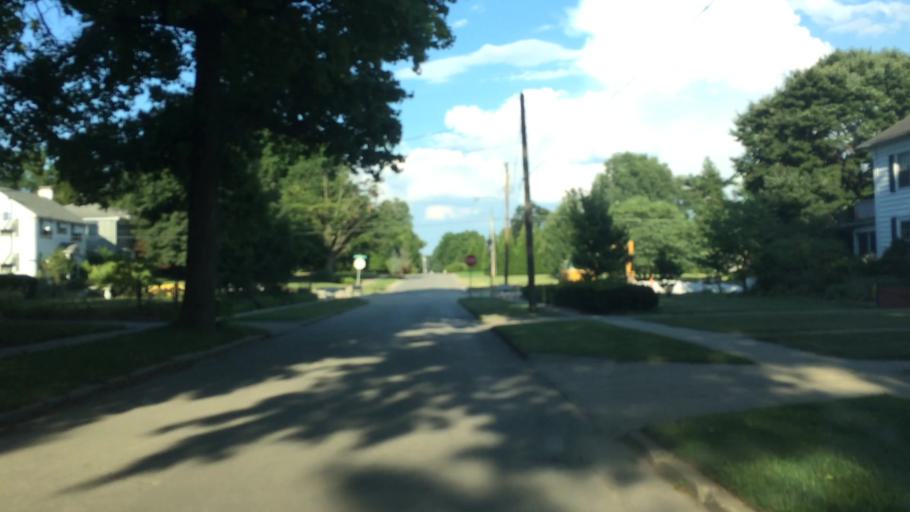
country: US
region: Missouri
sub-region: Greene County
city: Springfield
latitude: 37.1946
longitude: -93.2674
